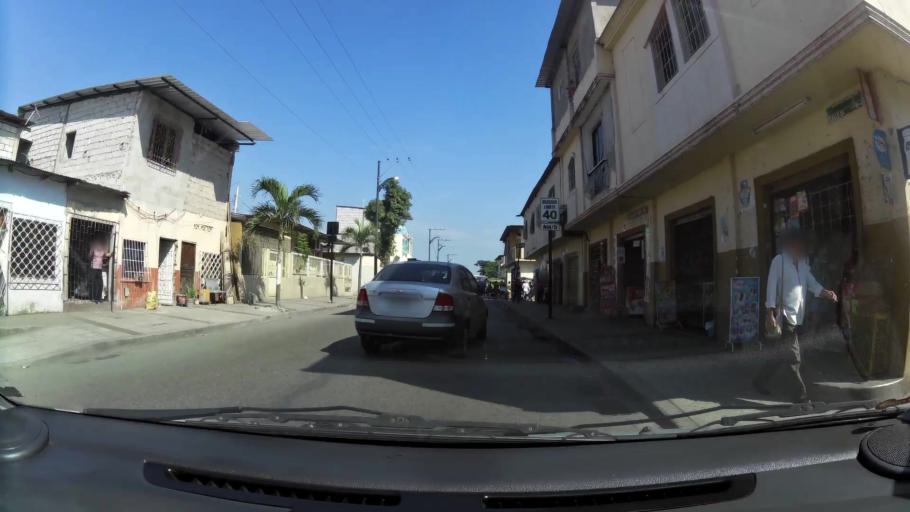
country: EC
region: Guayas
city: Eloy Alfaro
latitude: -2.1012
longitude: -79.9257
